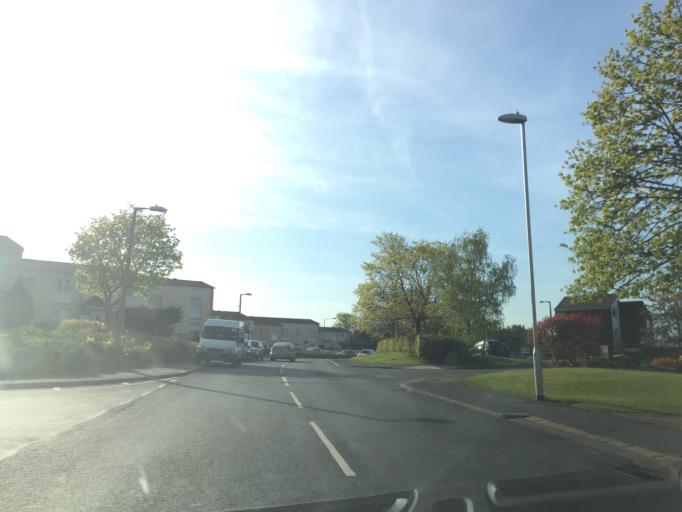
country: GB
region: England
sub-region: Essex
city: Harlow
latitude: 51.7510
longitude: 0.0819
